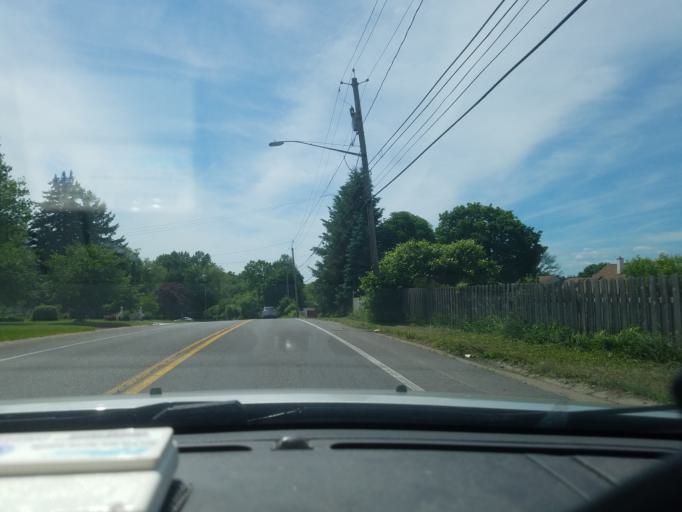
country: US
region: New York
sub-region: Onondaga County
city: East Syracuse
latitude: 43.0751
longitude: -76.0835
